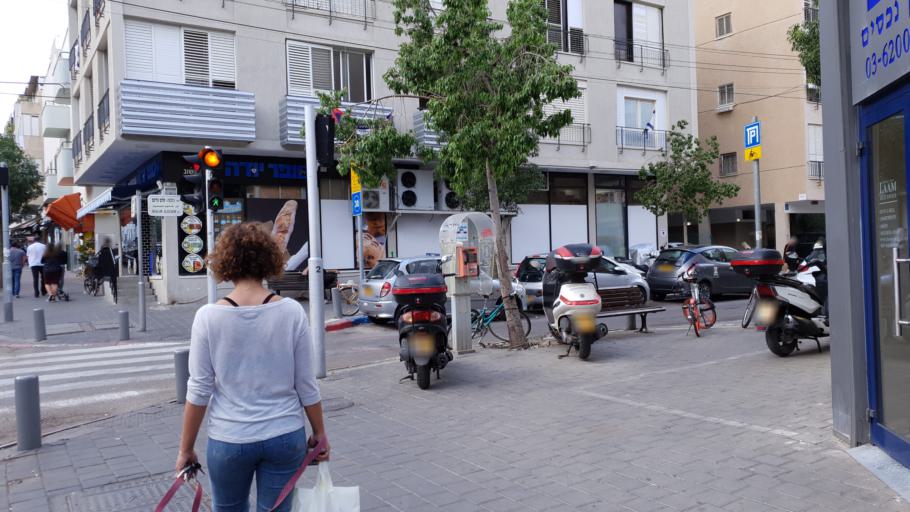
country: IL
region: Tel Aviv
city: Tel Aviv
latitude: 32.0770
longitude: 34.7697
